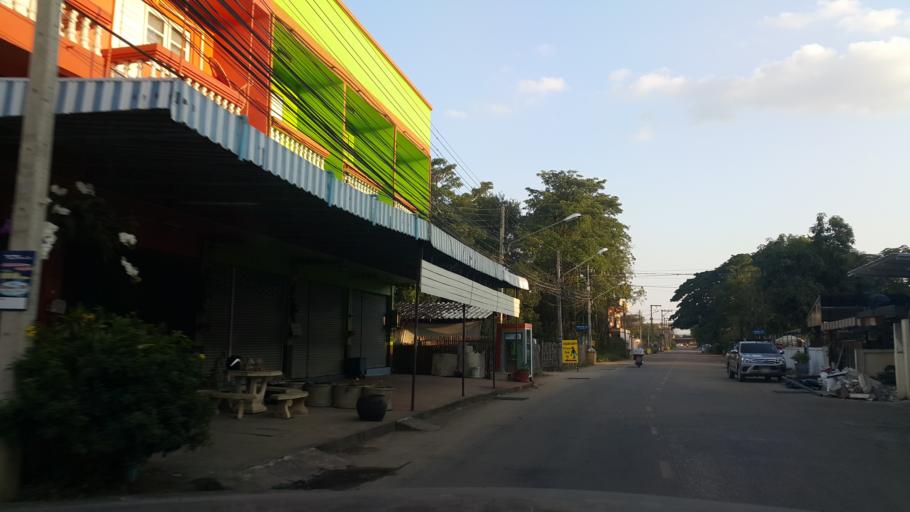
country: TH
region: Lampang
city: Lampang
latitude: 18.2719
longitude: 99.4717
